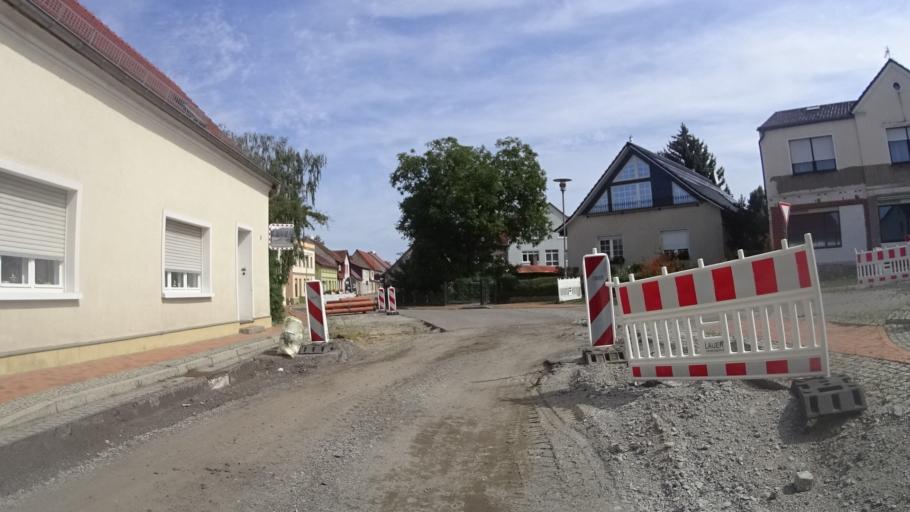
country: DE
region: Brandenburg
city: Gross Kreutz
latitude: 52.3163
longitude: 12.7414
